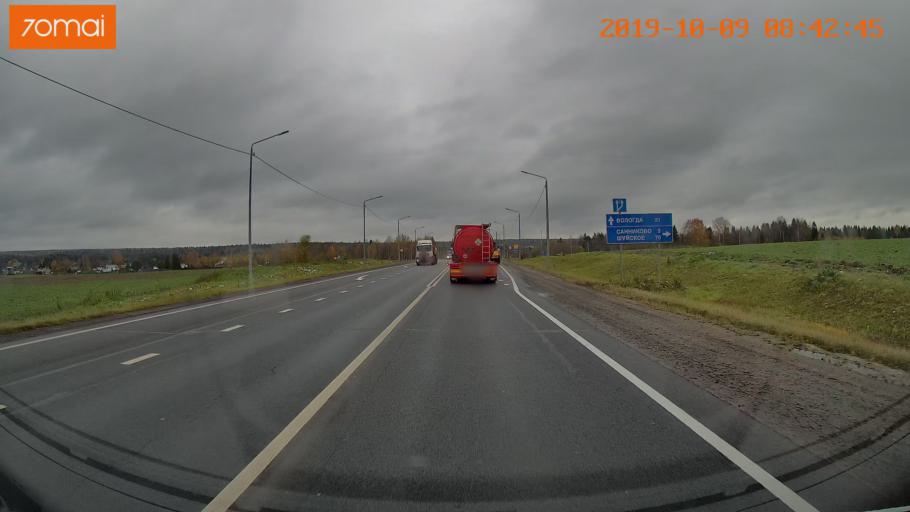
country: RU
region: Vologda
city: Gryazovets
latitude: 59.0184
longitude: 40.1172
